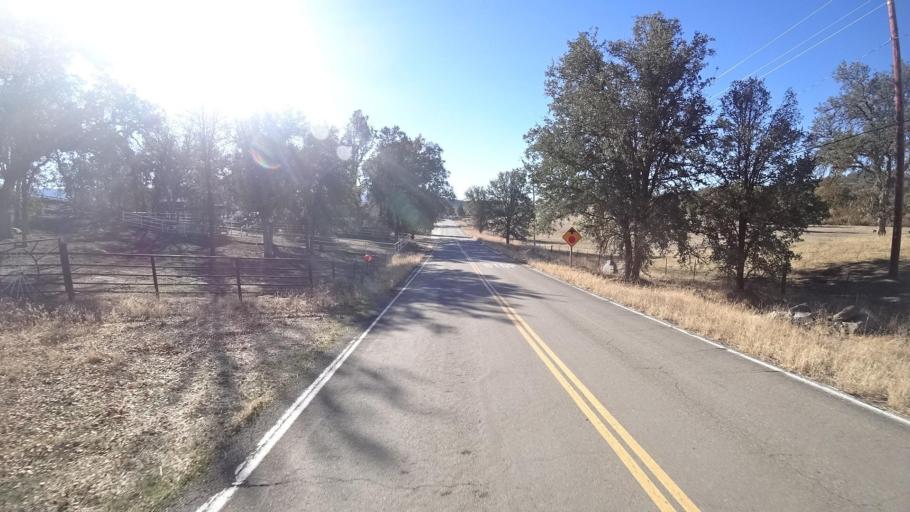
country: US
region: California
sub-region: Kern County
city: Alta Sierra
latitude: 35.7275
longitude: -118.7219
